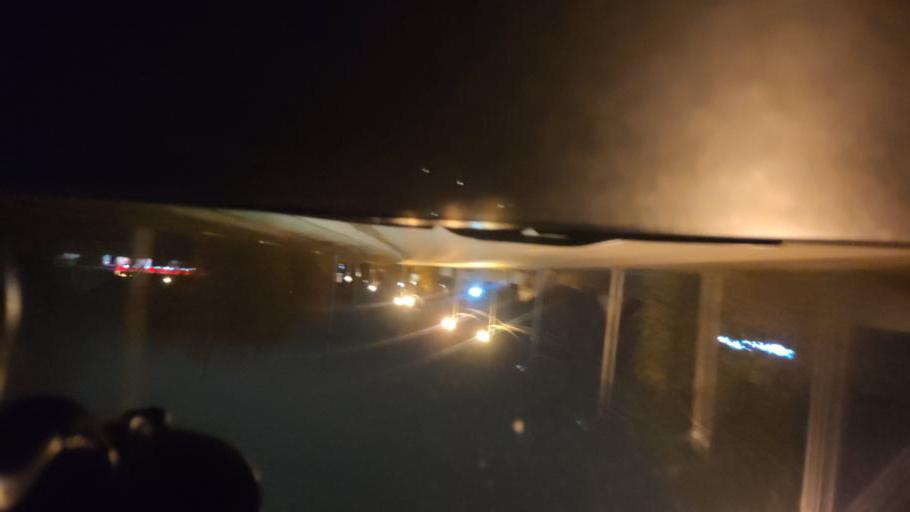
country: RU
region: Perm
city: Kondratovo
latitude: 57.9525
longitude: 56.1326
